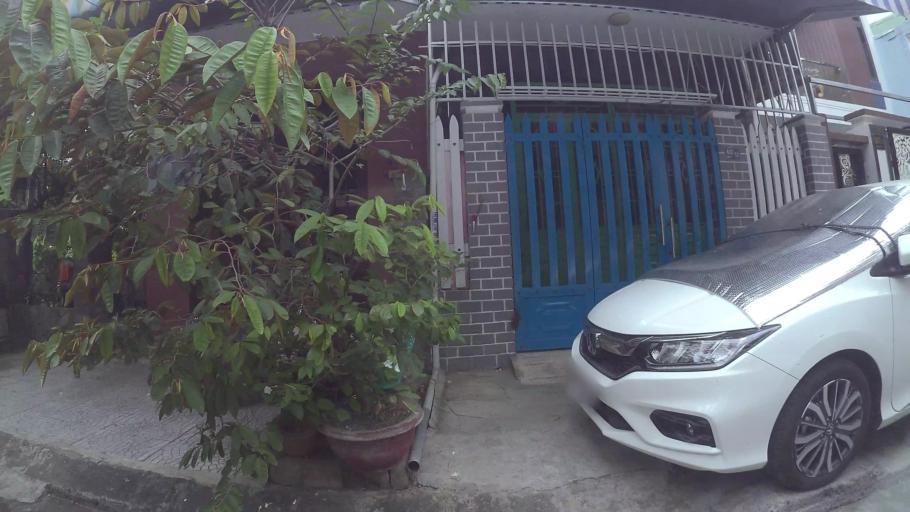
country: VN
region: Da Nang
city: Thanh Khe
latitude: 16.0581
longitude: 108.1871
